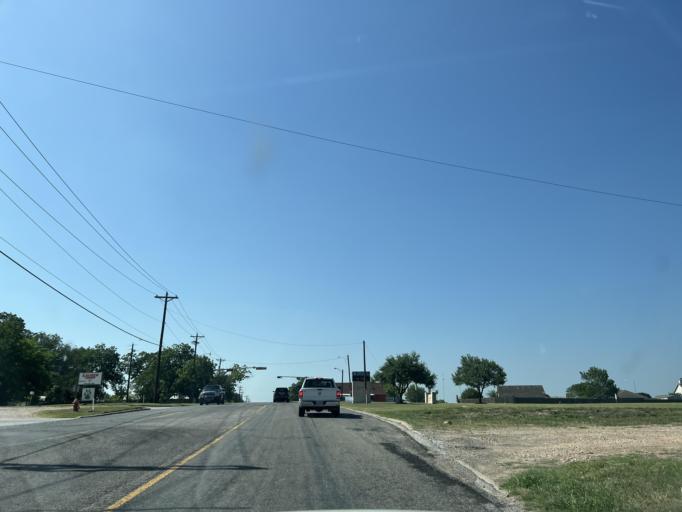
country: US
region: Texas
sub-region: Washington County
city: Brenham
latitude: 30.1803
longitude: -96.4015
